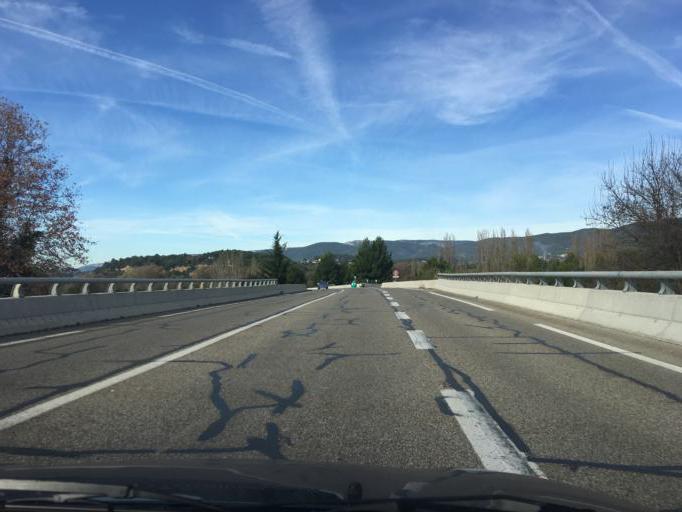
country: FR
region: Provence-Alpes-Cote d'Azur
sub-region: Departement du Vaucluse
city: Lauris
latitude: 43.7366
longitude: 5.3414
